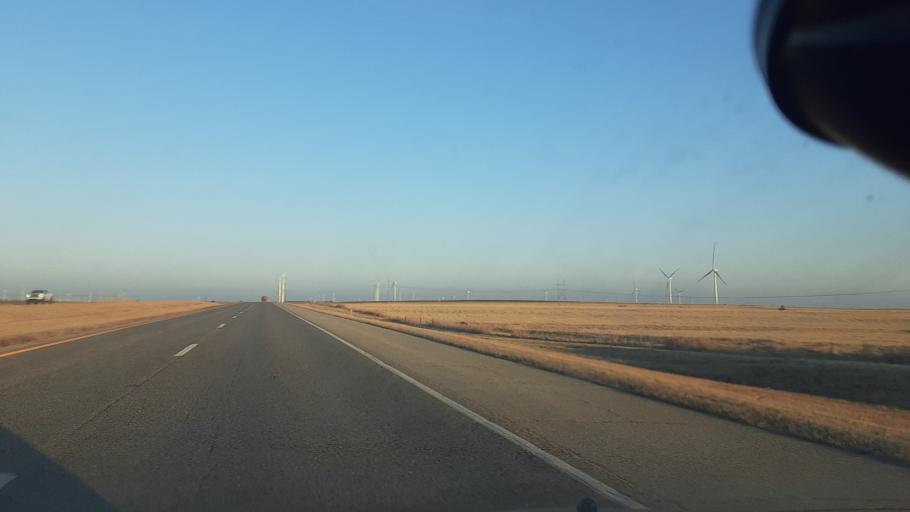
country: US
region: Oklahoma
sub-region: Noble County
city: Perry
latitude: 36.3975
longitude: -97.4873
